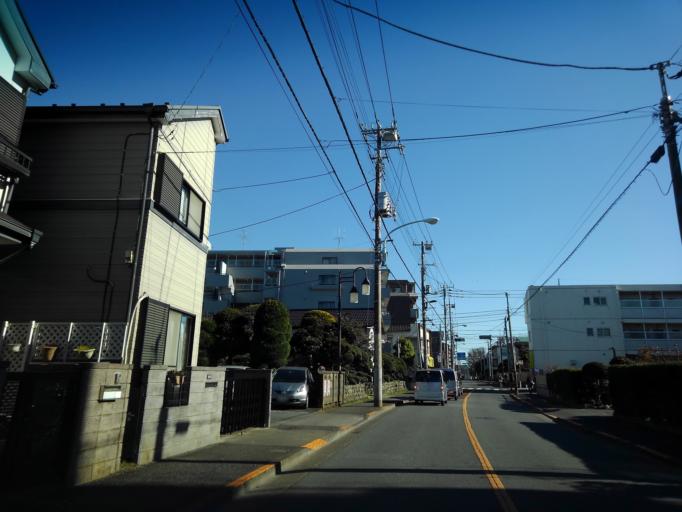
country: JP
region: Tokyo
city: Chofugaoka
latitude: 35.6668
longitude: 139.5131
